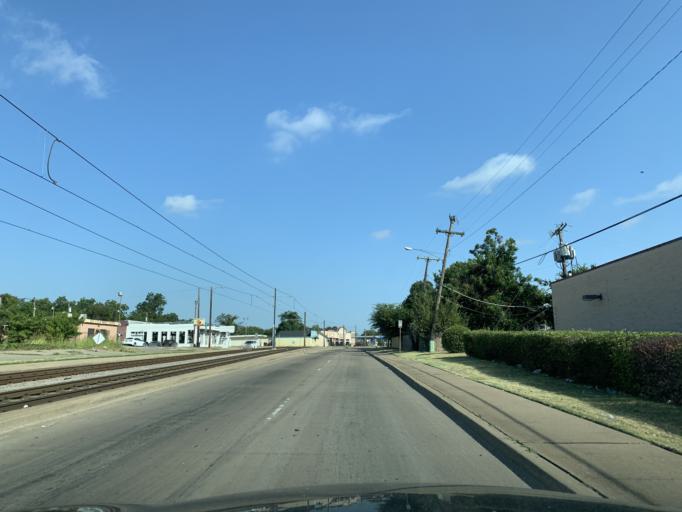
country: US
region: Texas
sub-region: Dallas County
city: Dallas
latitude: 32.7105
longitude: -96.8033
